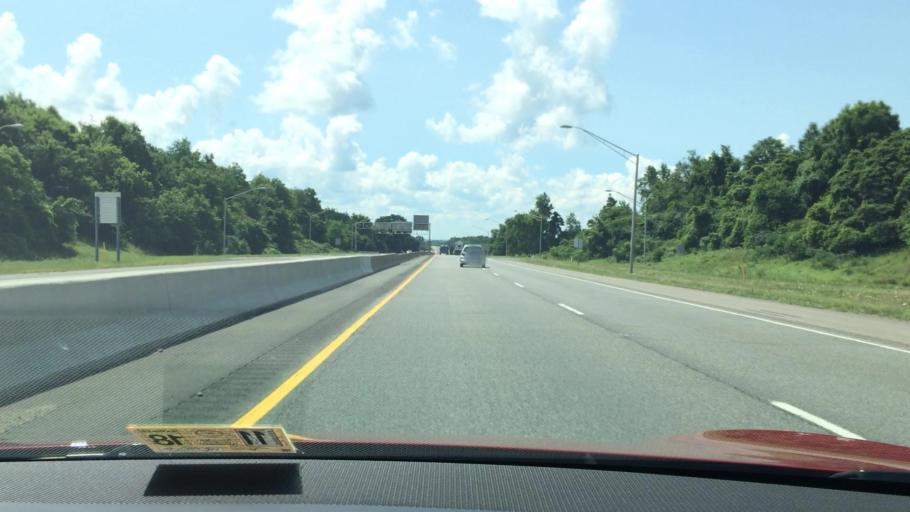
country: US
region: Indiana
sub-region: Saint Joseph County
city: South Bend
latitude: 41.7034
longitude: -86.3400
